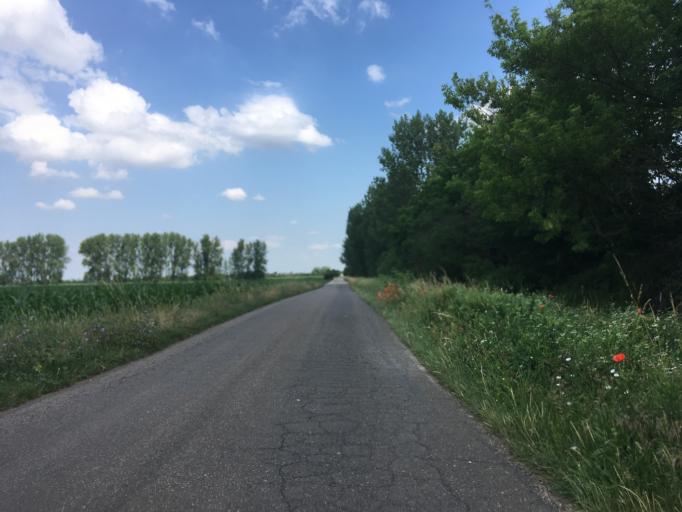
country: DE
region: Saxony-Anhalt
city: Osternienburg
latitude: 51.7600
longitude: 12.0634
